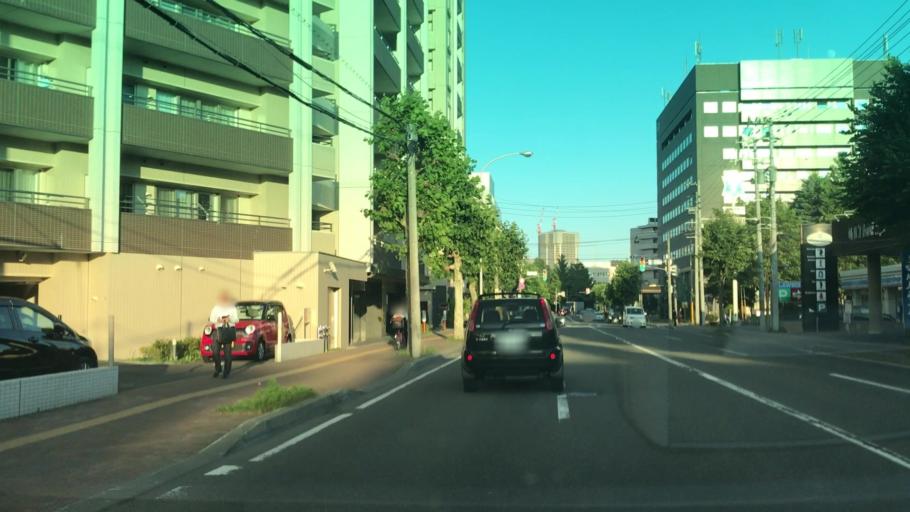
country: JP
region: Hokkaido
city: Sapporo
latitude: 43.0721
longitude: 141.3306
